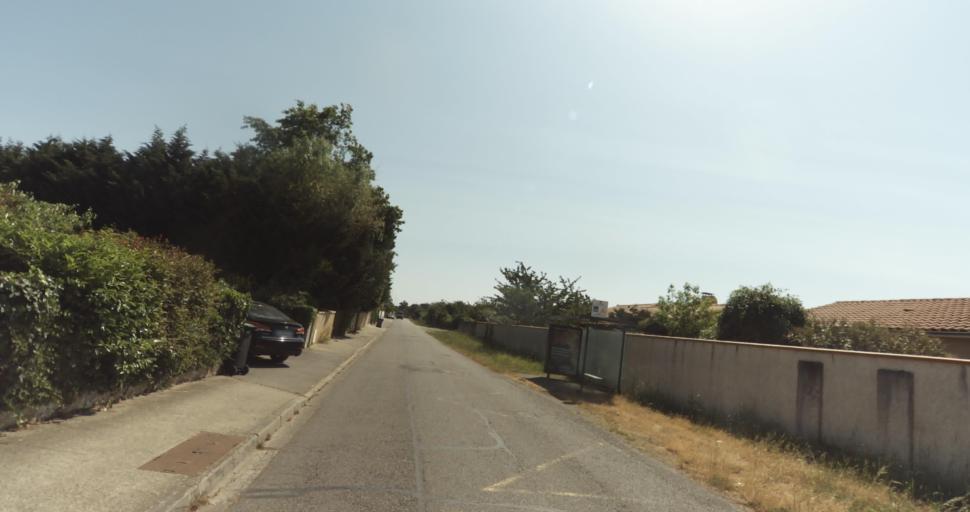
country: FR
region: Midi-Pyrenees
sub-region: Departement de la Haute-Garonne
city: La Salvetat-Saint-Gilles
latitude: 43.5789
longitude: 1.2822
